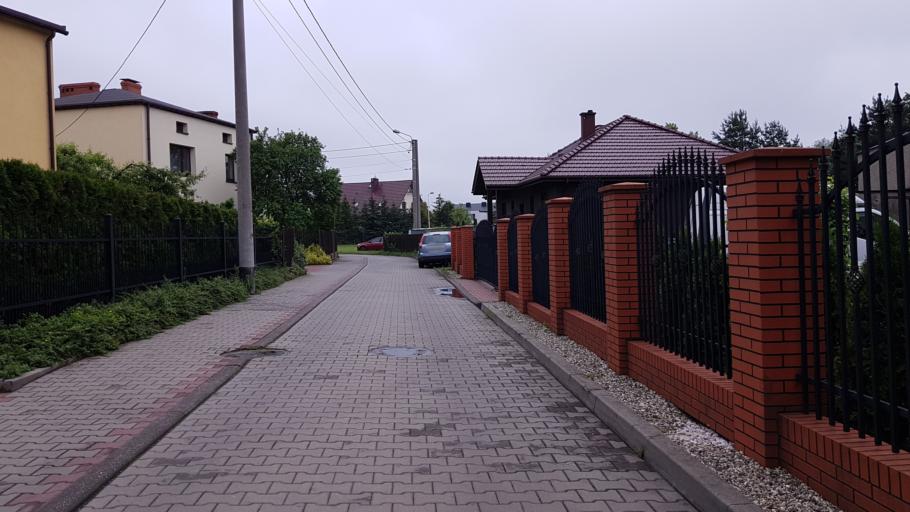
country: PL
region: Silesian Voivodeship
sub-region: Tychy
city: Tychy
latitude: 50.1089
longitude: 18.9585
